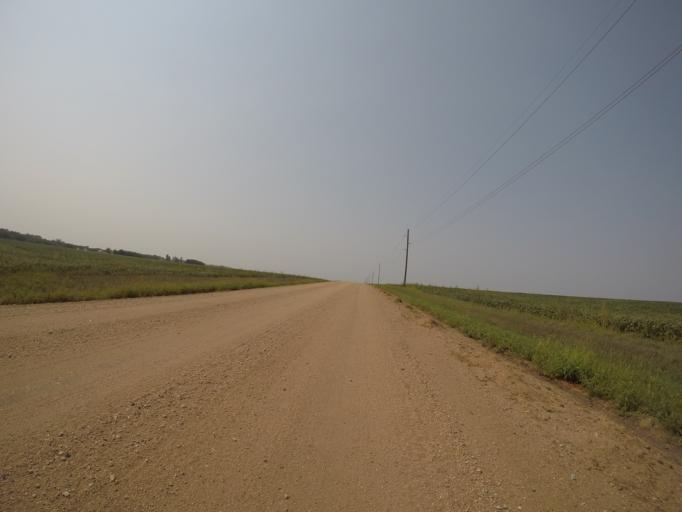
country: US
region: Nebraska
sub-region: Gage County
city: Beatrice
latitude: 40.2774
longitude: -96.8149
